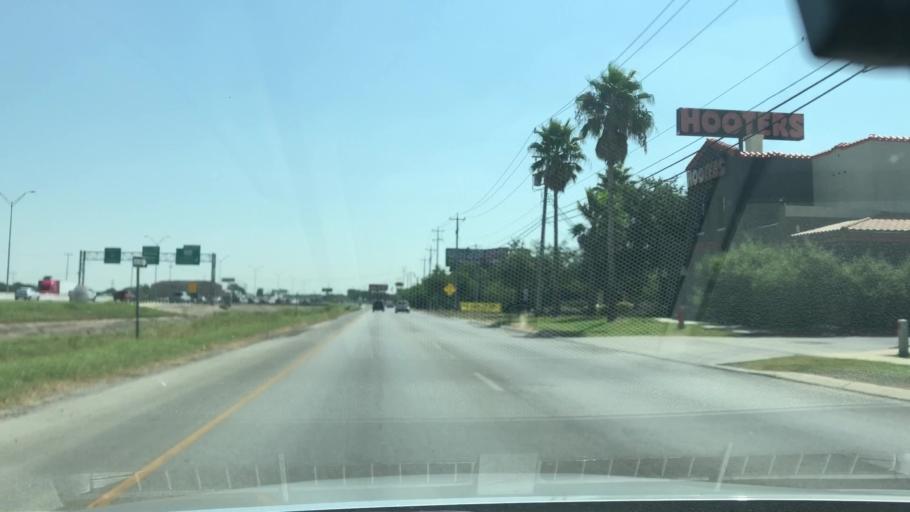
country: US
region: Texas
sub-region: Bexar County
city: Selma
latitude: 29.5805
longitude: -98.3176
